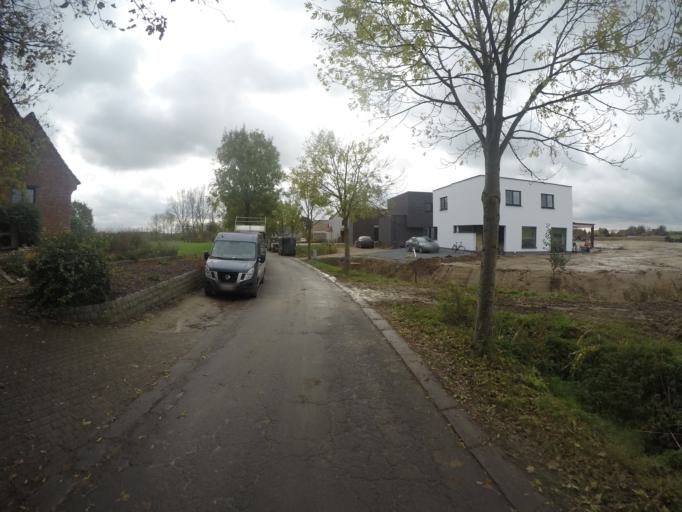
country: BE
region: Flanders
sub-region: Provincie Oost-Vlaanderen
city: Hamme
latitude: 51.1200
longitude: 4.1347
